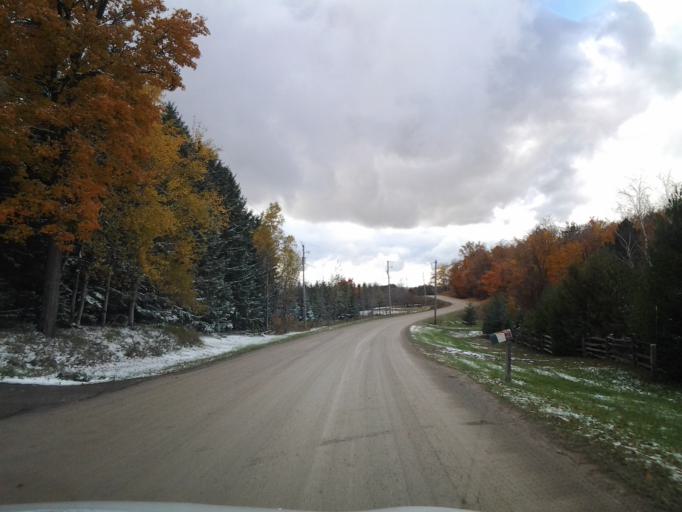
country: CA
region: Ontario
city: Shelburne
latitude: 44.0590
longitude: -80.1044
